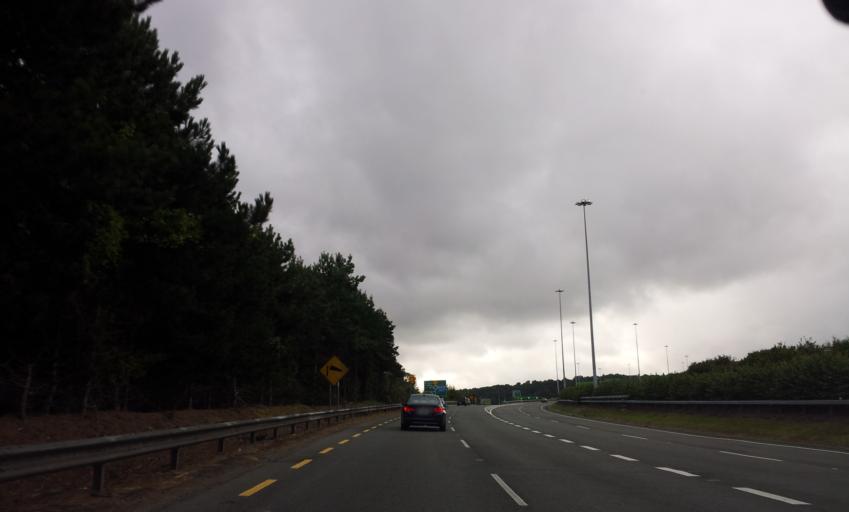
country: IE
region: Munster
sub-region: County Cork
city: Passage West
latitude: 51.9028
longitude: -8.3801
